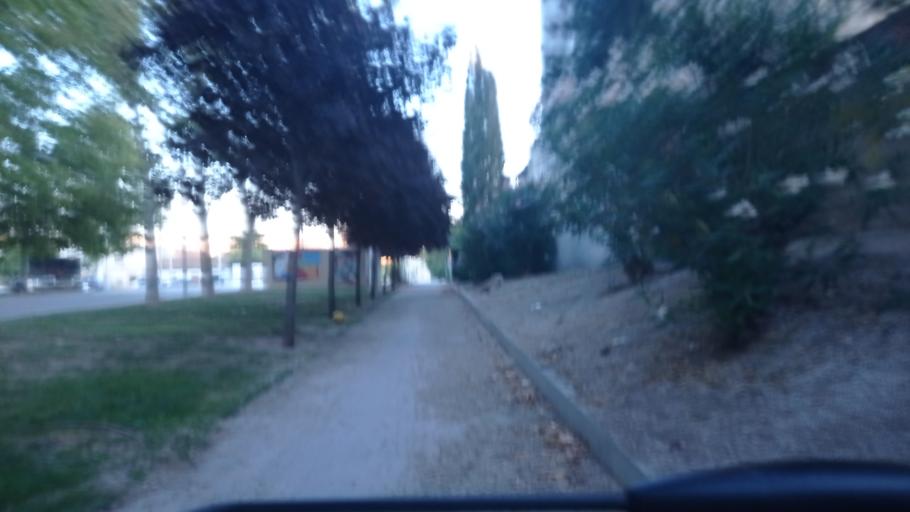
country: ES
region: Aragon
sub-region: Provincia de Zaragoza
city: Oliver-Valdefierro, Oliver, Valdefierro
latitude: 41.6512
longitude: -0.9245
